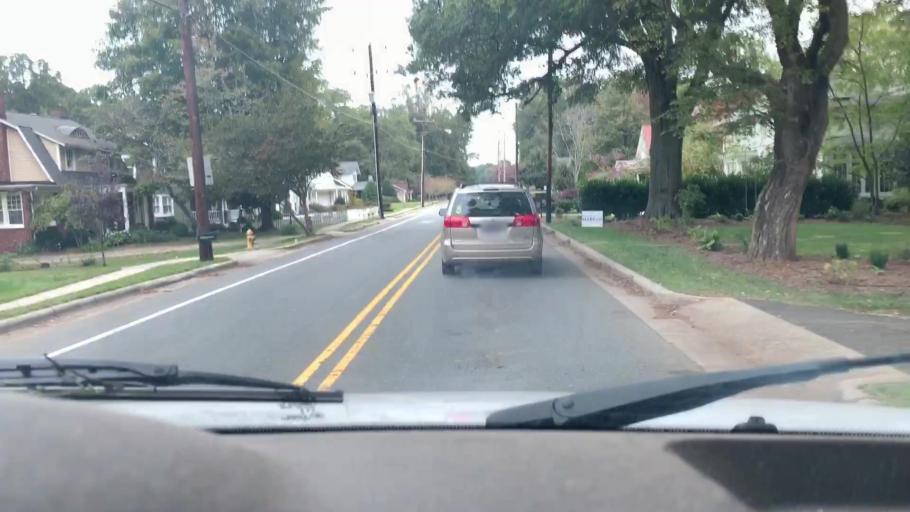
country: US
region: North Carolina
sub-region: Gaston County
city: Davidson
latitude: 35.5056
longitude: -80.8451
